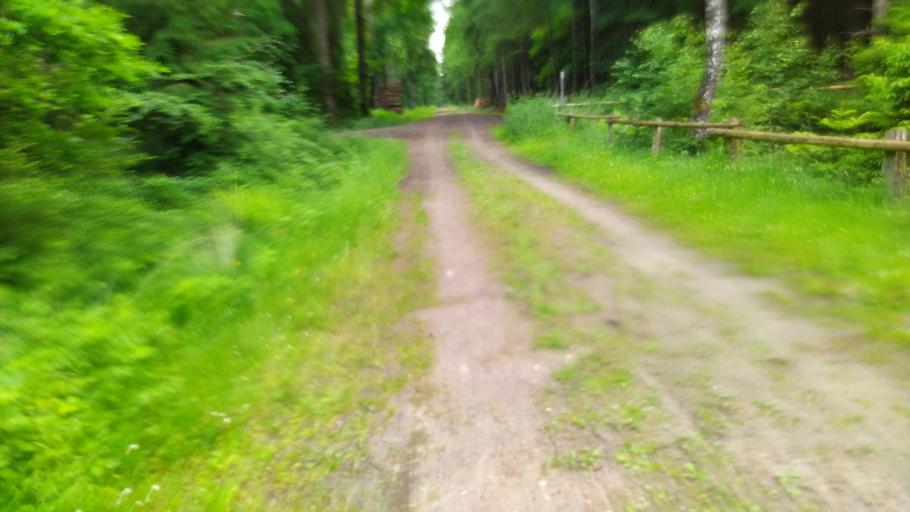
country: DE
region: Lower Saxony
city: Deinstedt
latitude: 53.4389
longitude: 9.2431
